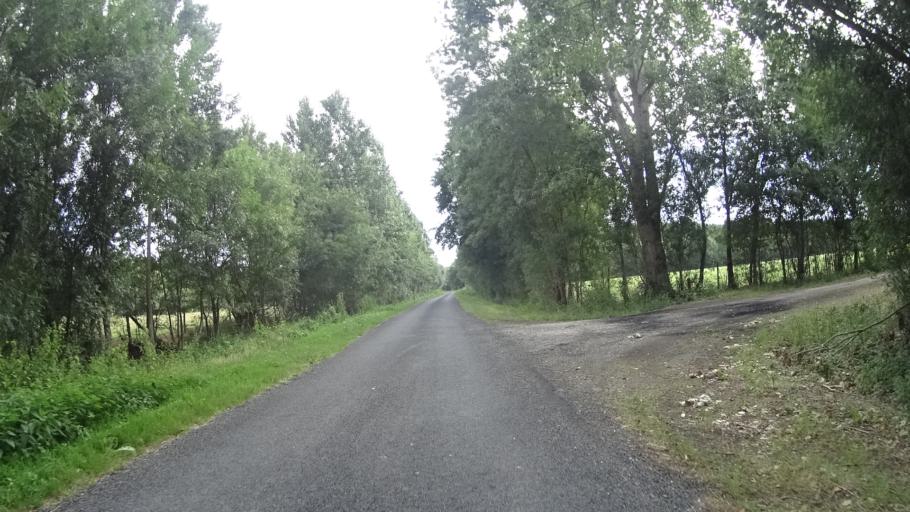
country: FR
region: Centre
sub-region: Departement d'Indre-et-Loire
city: Chouze-sur-Loire
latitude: 47.2083
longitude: 0.1128
